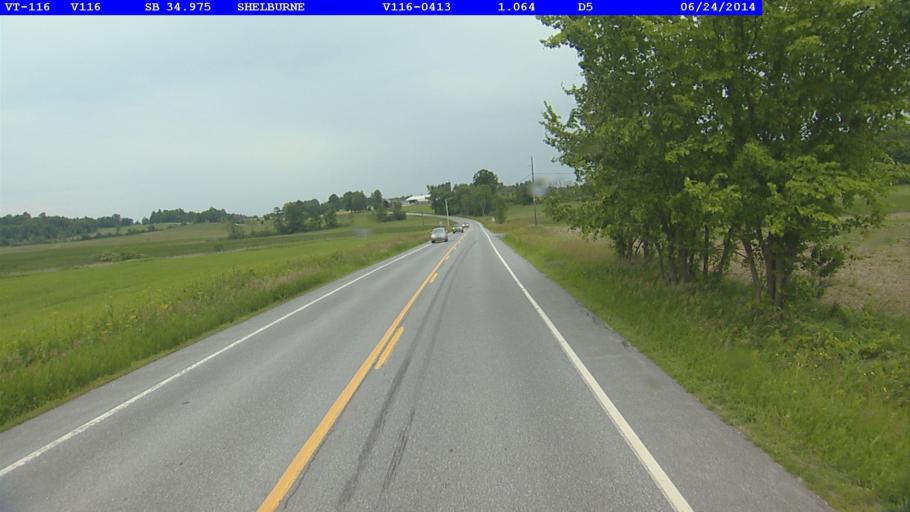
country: US
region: Vermont
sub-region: Chittenden County
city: Hinesburg
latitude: 44.3939
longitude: -73.1406
